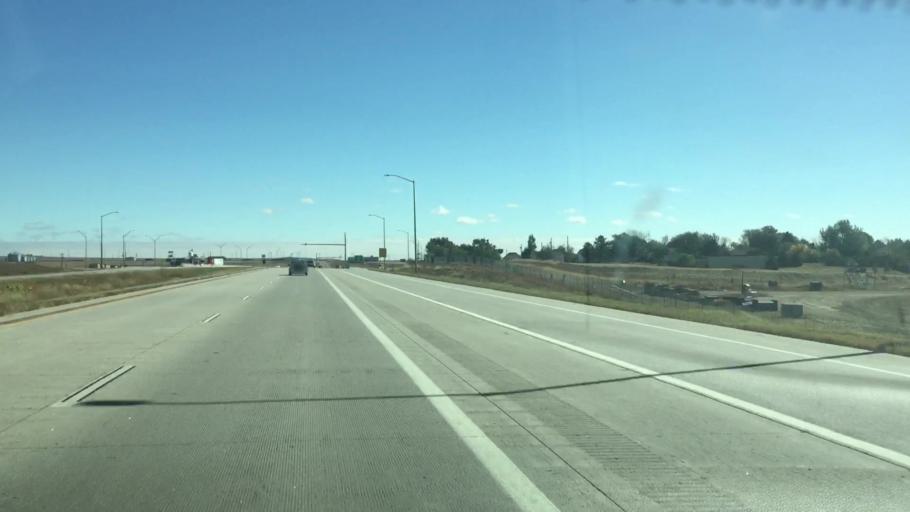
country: US
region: Colorado
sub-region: Lincoln County
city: Limon
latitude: 39.2732
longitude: -103.6904
